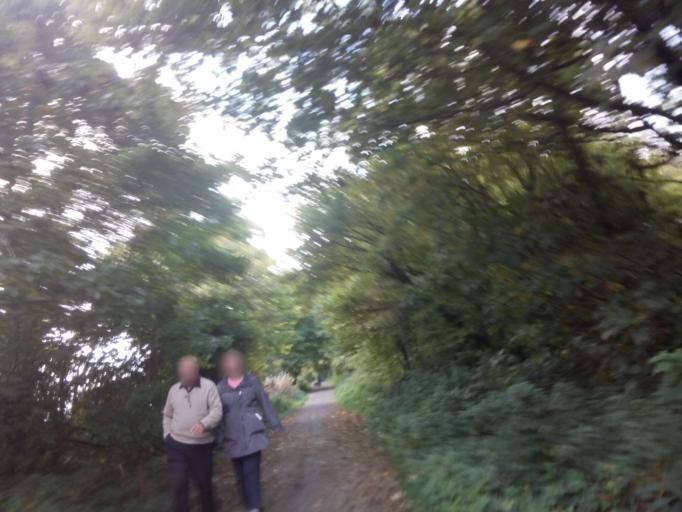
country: GB
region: England
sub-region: County Durham
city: Pittington
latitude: 54.7812
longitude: -1.5179
